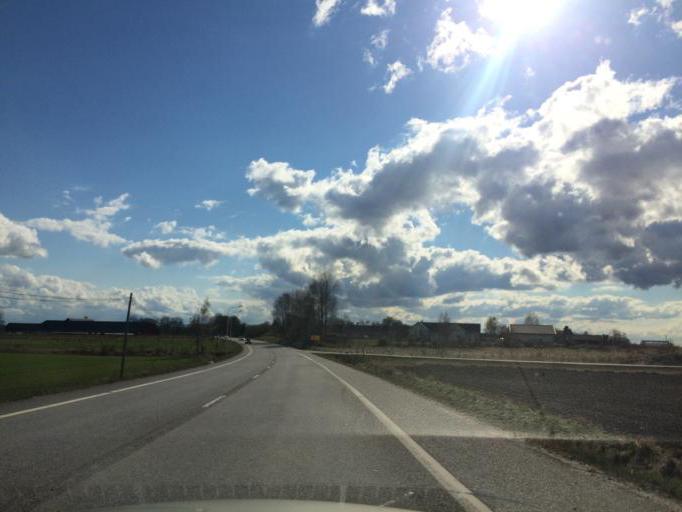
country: SE
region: Soedermanland
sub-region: Eskilstuna Kommun
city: Eskilstuna
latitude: 59.4293
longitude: 16.6125
